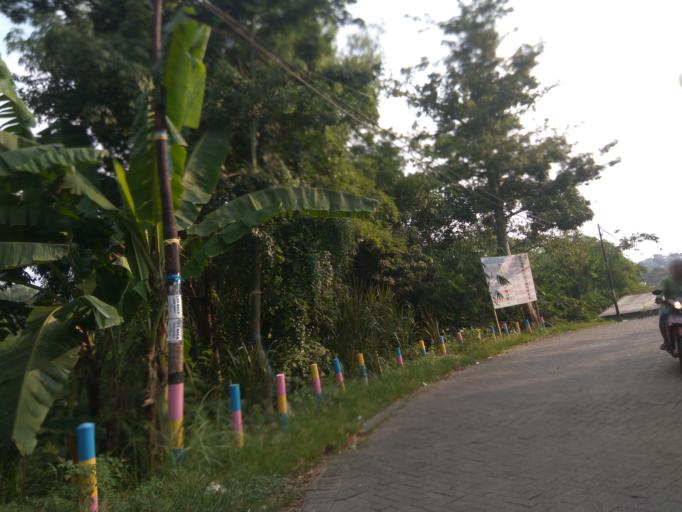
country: ID
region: Central Java
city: Semarang
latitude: -7.0173
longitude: 110.3841
